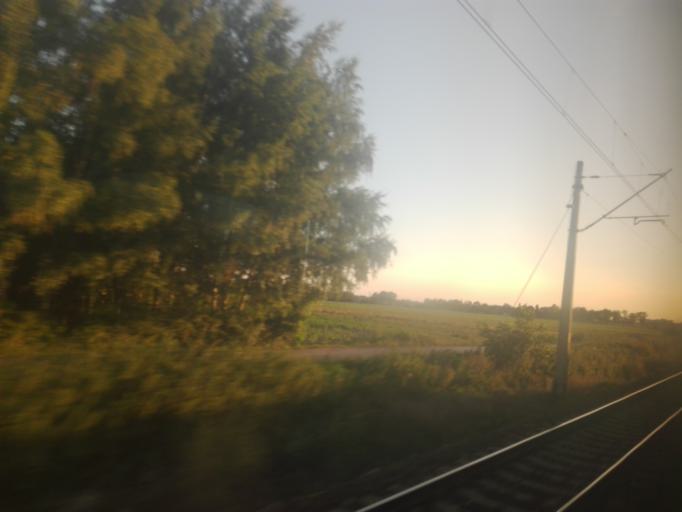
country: PL
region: Masovian Voivodeship
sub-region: Powiat warszawski zachodni
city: Ozarow Mazowiecki
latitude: 52.2084
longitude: 20.7641
